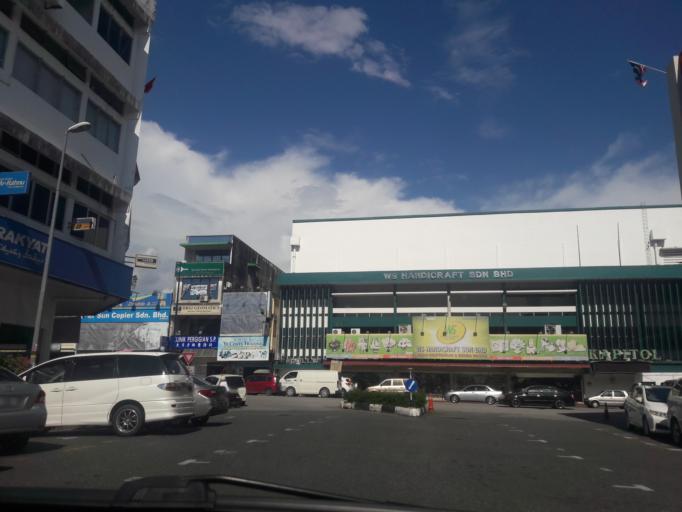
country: MY
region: Kedah
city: Sungai Petani
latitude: 5.6407
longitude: 100.4868
